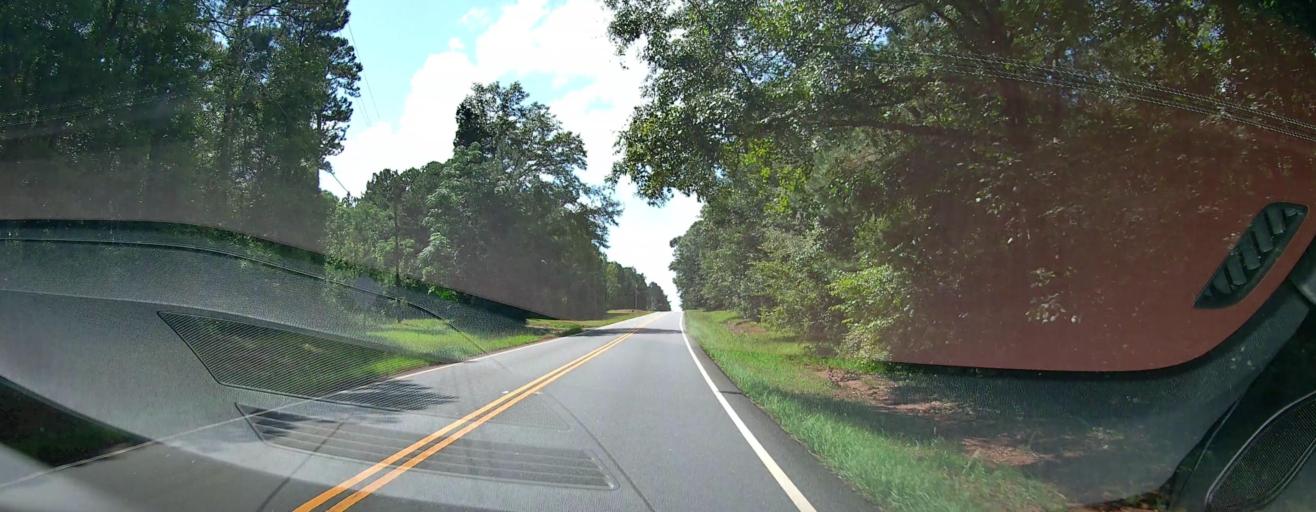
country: US
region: Georgia
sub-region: Crawford County
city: Knoxville
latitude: 32.8733
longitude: -83.9874
